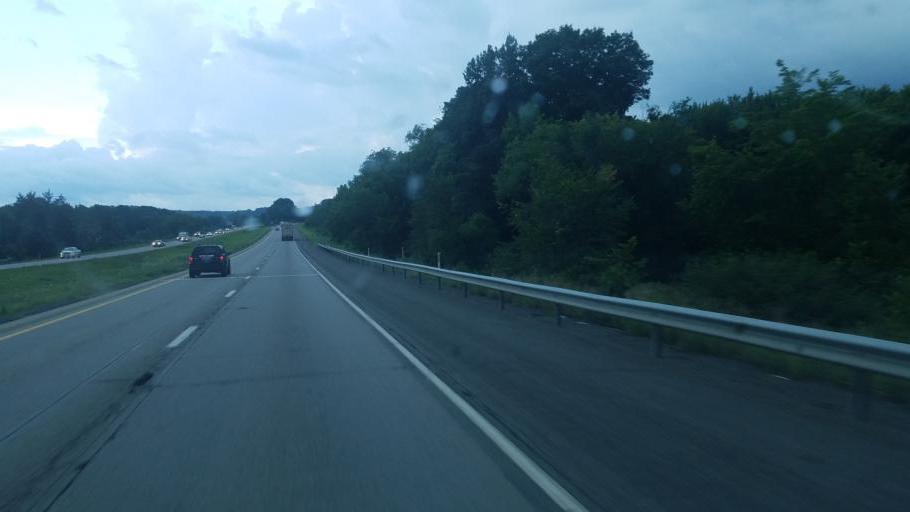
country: US
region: Pennsylvania
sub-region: Butler County
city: Slippery Rock
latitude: 41.0171
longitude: -80.1153
